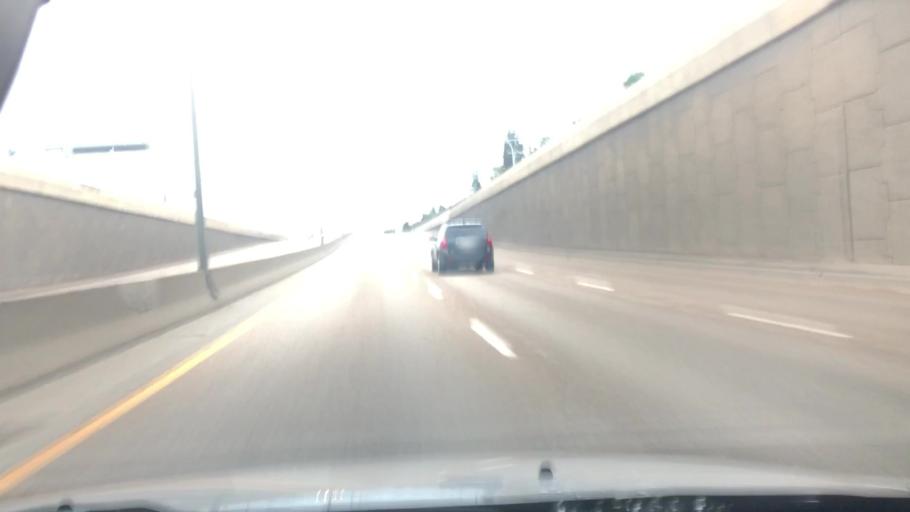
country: CA
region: Alberta
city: Edmonton
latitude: 53.5813
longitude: -113.4915
